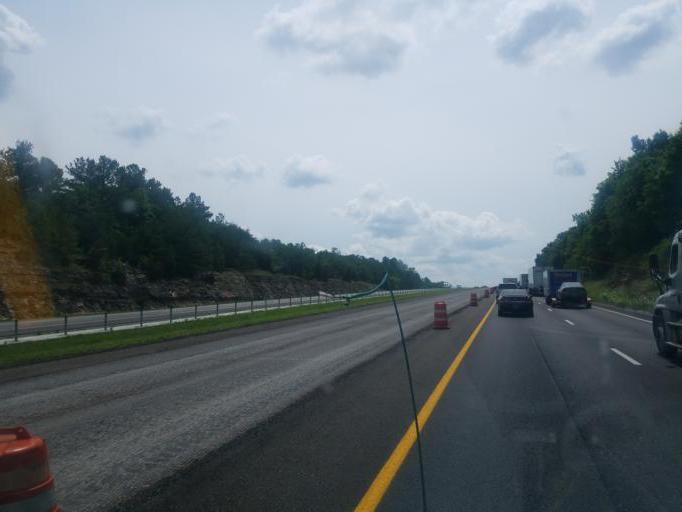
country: US
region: Kentucky
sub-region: Hardin County
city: Elizabethtown
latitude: 37.7337
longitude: -85.8115
